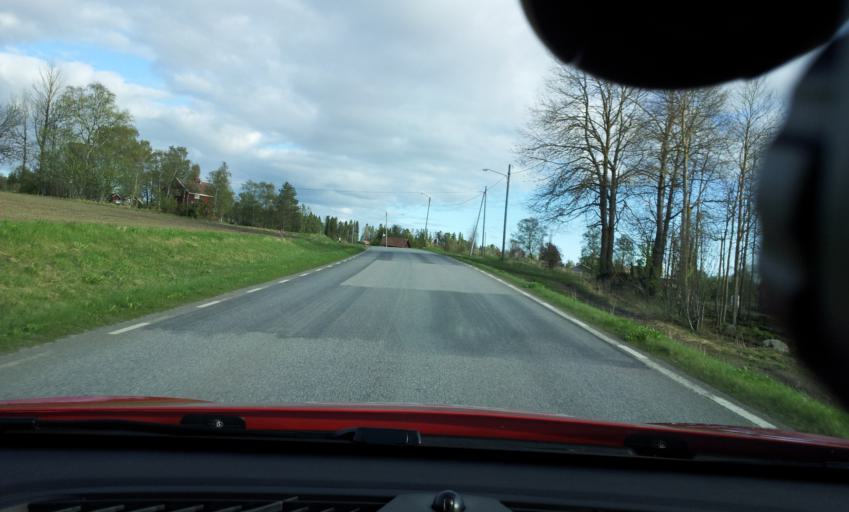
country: SE
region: Jaemtland
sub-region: Krokoms Kommun
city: Krokom
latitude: 63.2550
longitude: 14.4094
